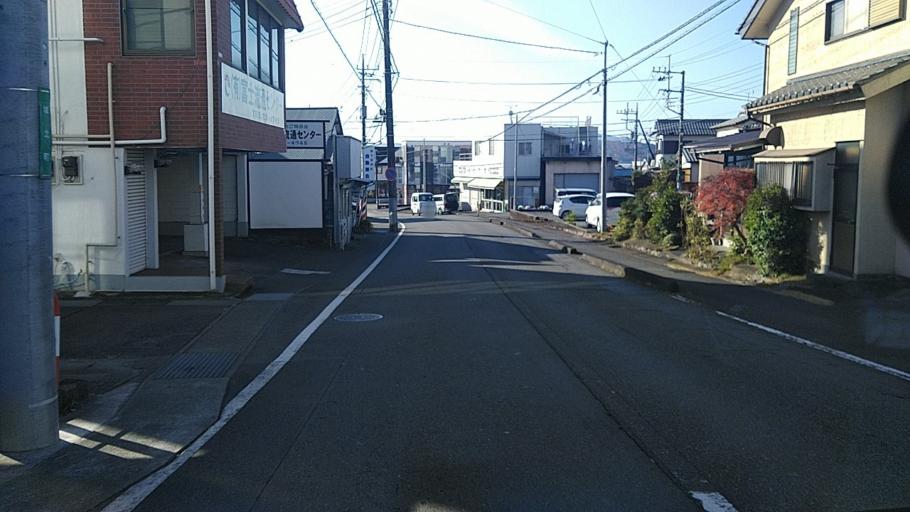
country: JP
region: Shizuoka
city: Fujinomiya
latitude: 35.2349
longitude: 138.6174
